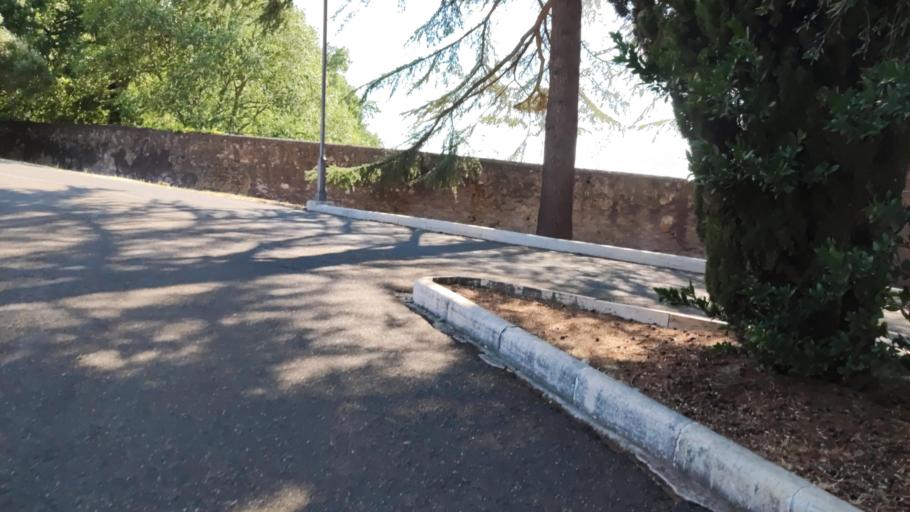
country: IT
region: Latium
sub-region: Citta metropolitana di Roma Capitale
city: Villa Adriana
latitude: 41.9454
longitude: 12.7721
